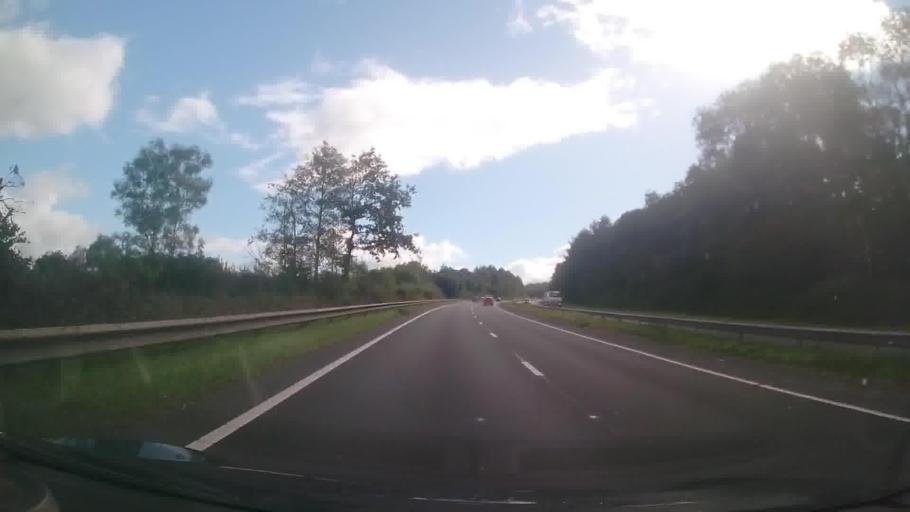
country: GB
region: Wales
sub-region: Carmarthenshire
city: Carmarthen
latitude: 51.8430
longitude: -4.2549
